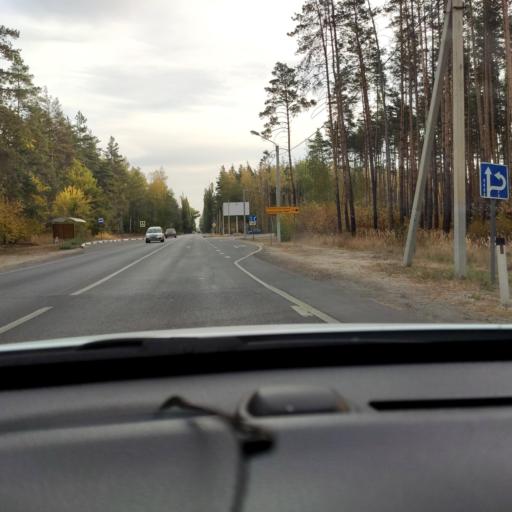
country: RU
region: Voronezj
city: Somovo
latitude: 51.6951
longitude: 39.3107
